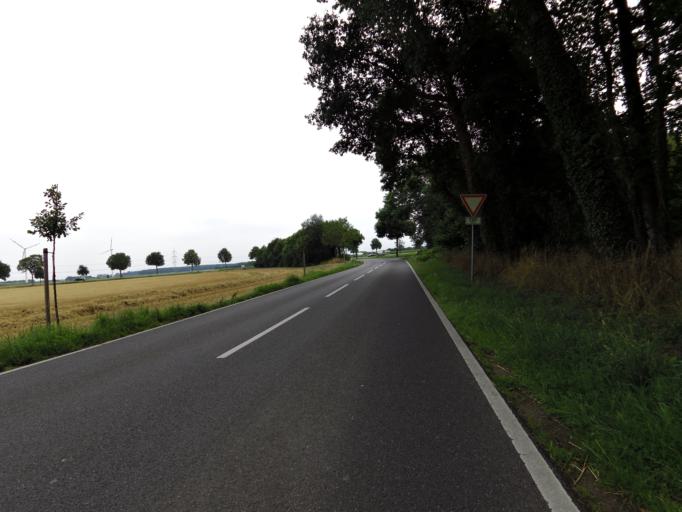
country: DE
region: North Rhine-Westphalia
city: Geilenkirchen
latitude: 51.0028
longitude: 6.1171
